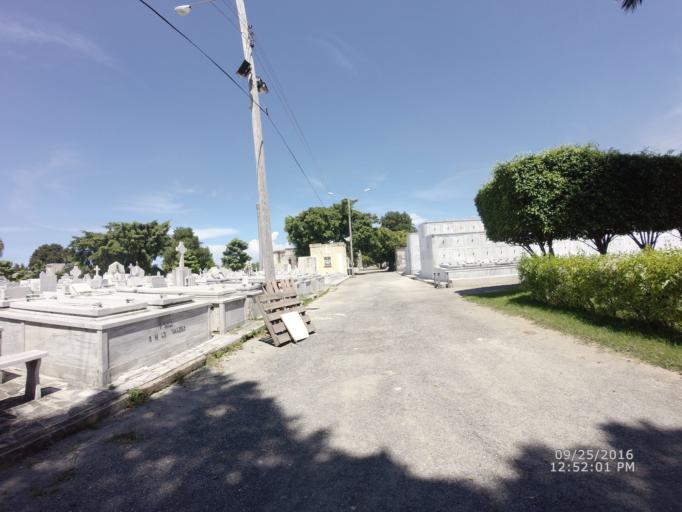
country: CU
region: La Habana
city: Havana
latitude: 23.1209
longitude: -82.3995
